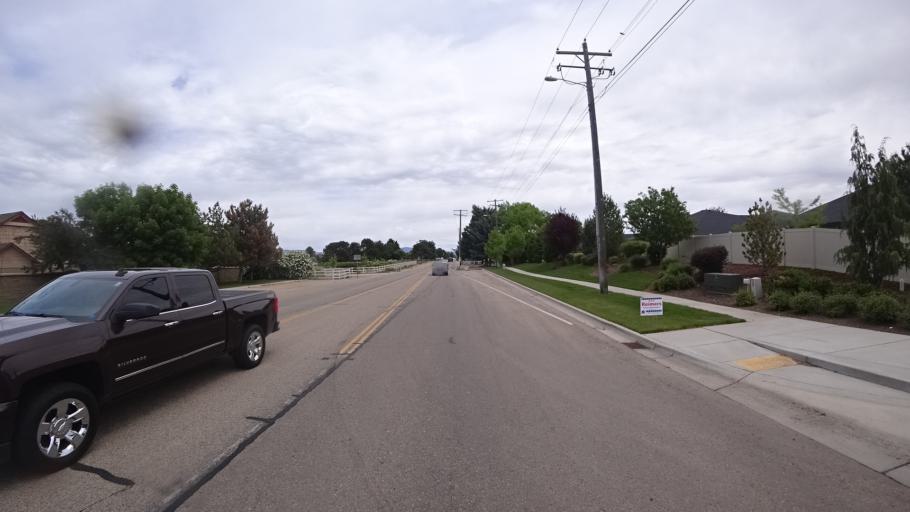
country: US
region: Idaho
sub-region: Ada County
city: Meridian
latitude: 43.5757
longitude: -116.3498
